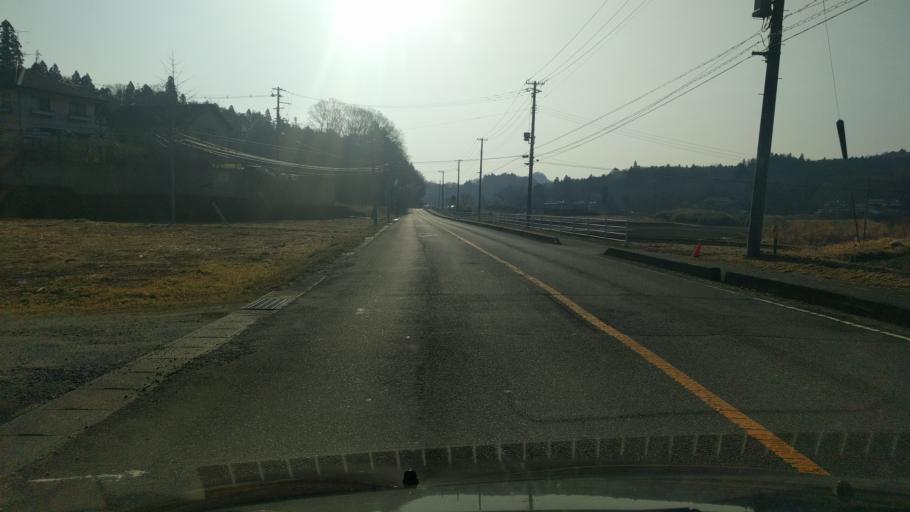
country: JP
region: Fukushima
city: Iwaki
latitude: 37.0465
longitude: 140.7987
